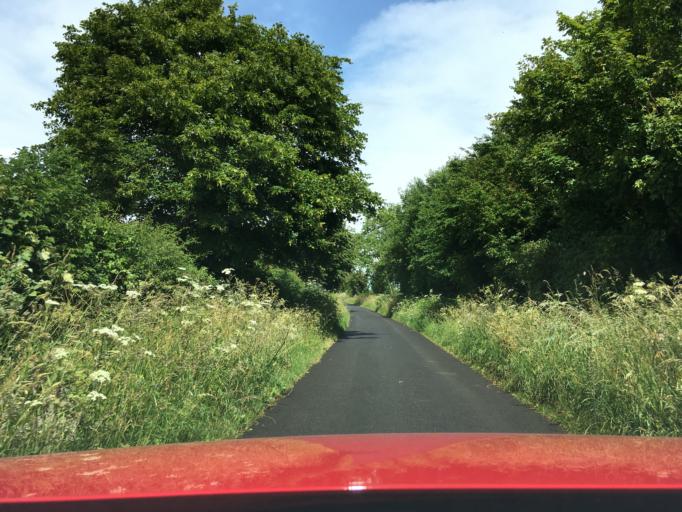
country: GB
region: England
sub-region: Gloucestershire
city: Tetbury
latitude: 51.6285
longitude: -2.2103
